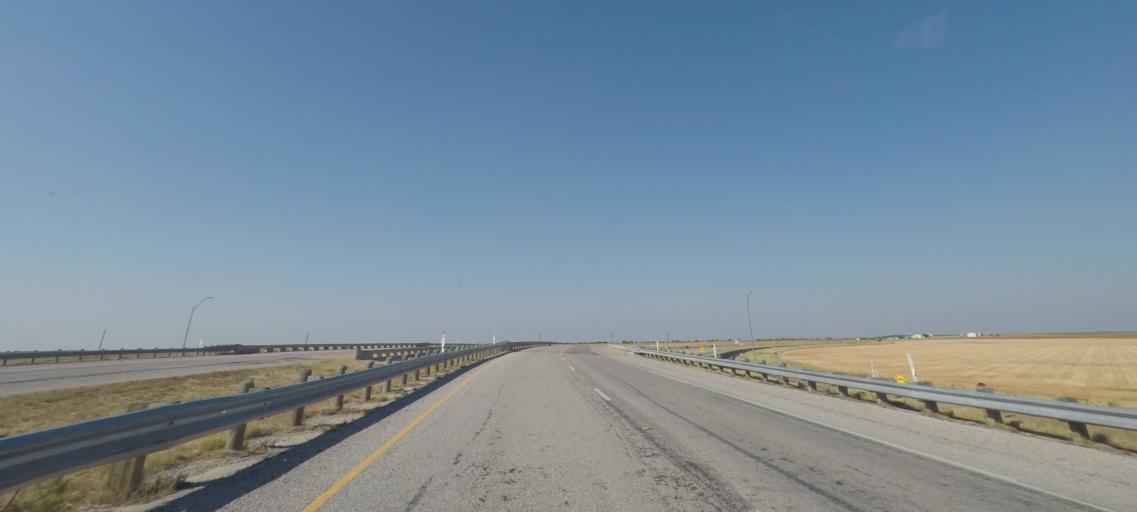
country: US
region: Texas
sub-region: Baylor County
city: Seymour
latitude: 33.6145
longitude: -99.2430
